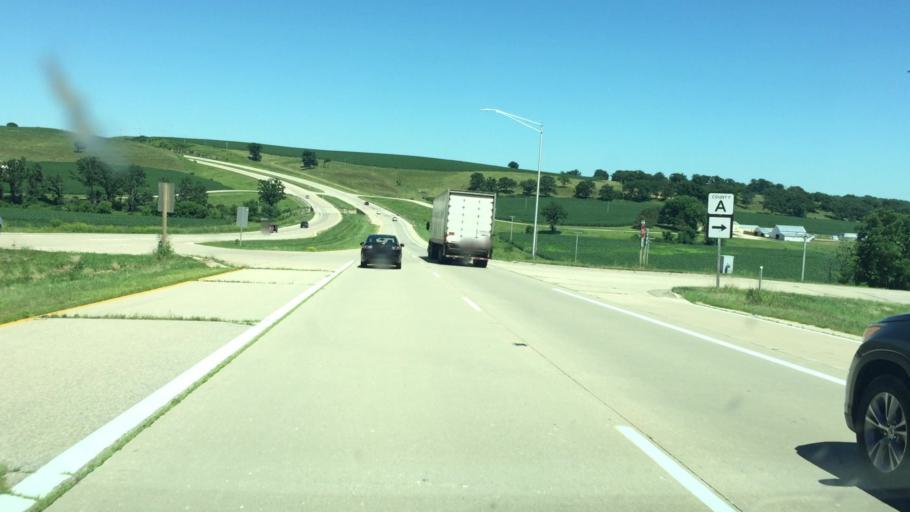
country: US
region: Wisconsin
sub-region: Iowa County
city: Mineral Point
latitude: 42.8237
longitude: -90.2464
